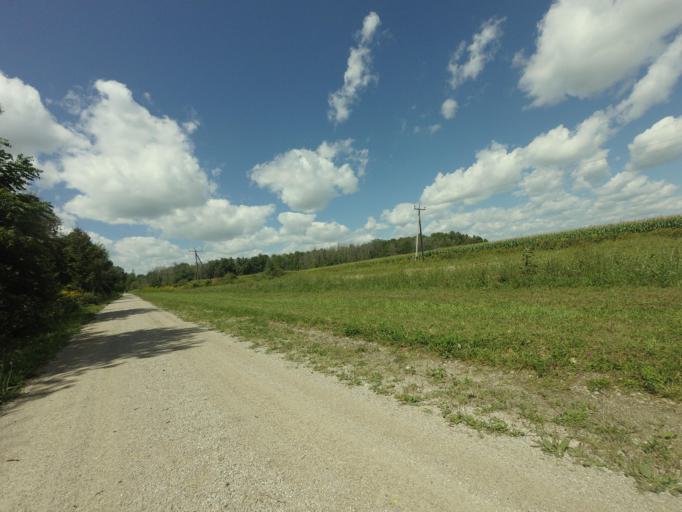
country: CA
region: Ontario
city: North Perth
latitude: 43.5919
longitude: -81.0860
